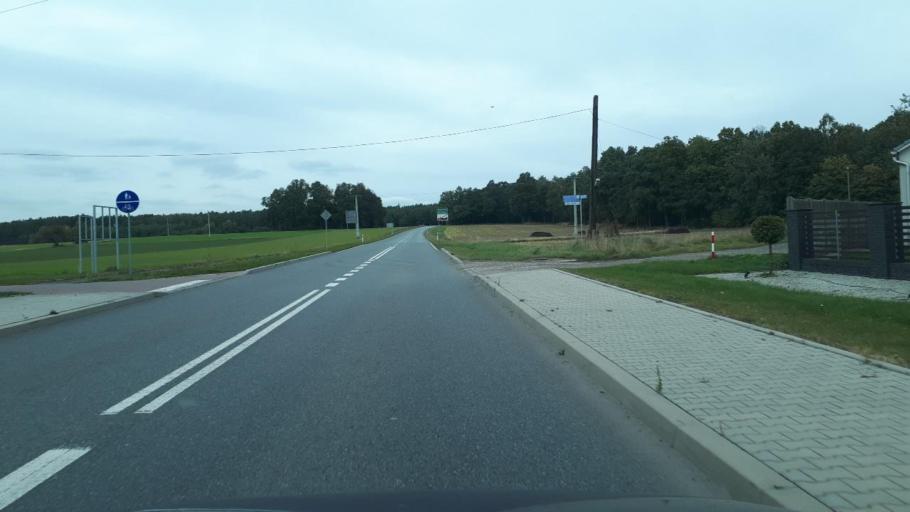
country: PL
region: Opole Voivodeship
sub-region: Powiat oleski
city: Dobrodzien
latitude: 50.7620
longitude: 18.4304
